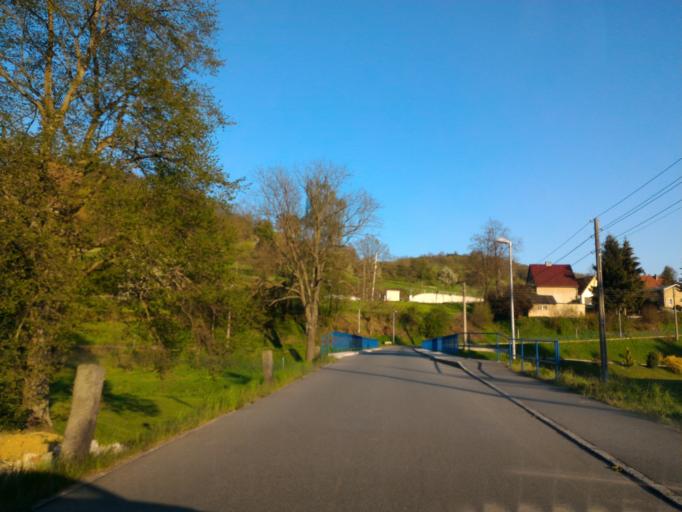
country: DE
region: Saxony
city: Hainewalde
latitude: 50.9208
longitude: 14.7176
